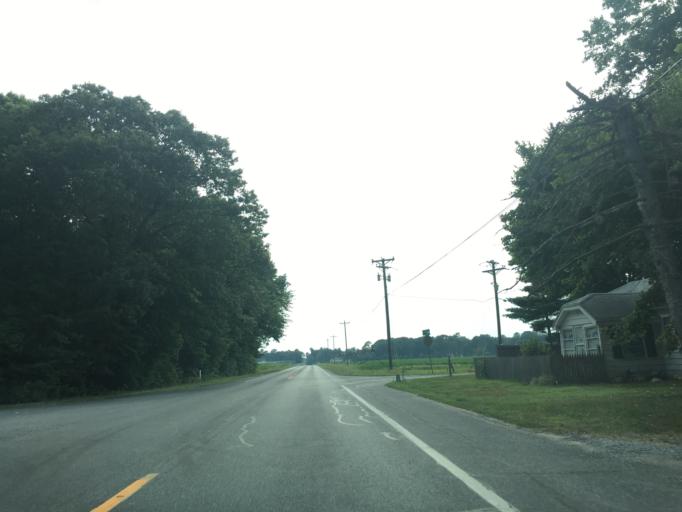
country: US
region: Delaware
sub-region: Sussex County
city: Bridgeville
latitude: 38.7501
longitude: -75.5411
